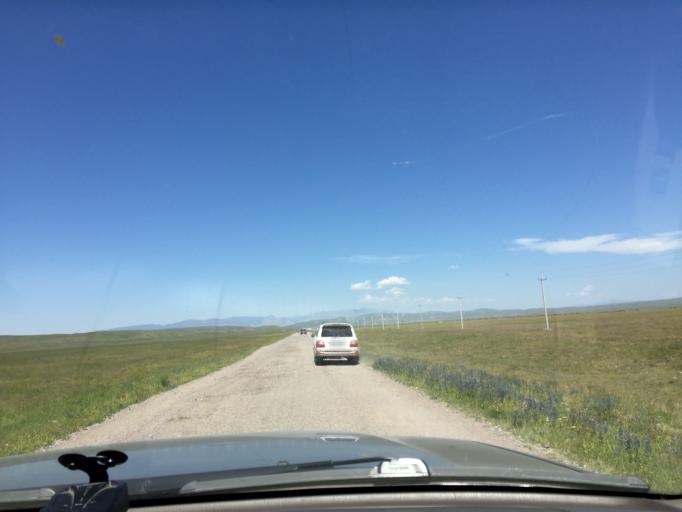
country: KZ
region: Almaty Oblysy
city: Kegen
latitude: 42.7869
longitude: 79.1652
